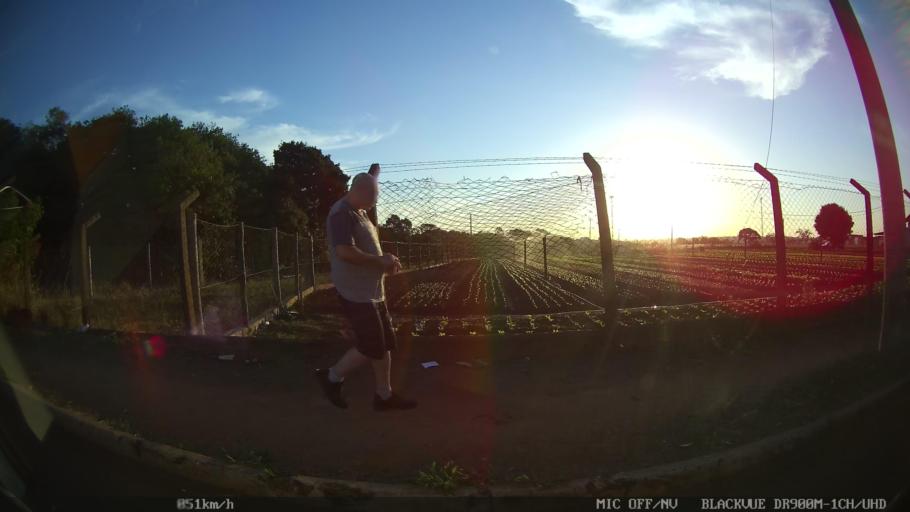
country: BR
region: Sao Paulo
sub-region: Franca
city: Franca
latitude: -20.4967
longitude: -47.4072
